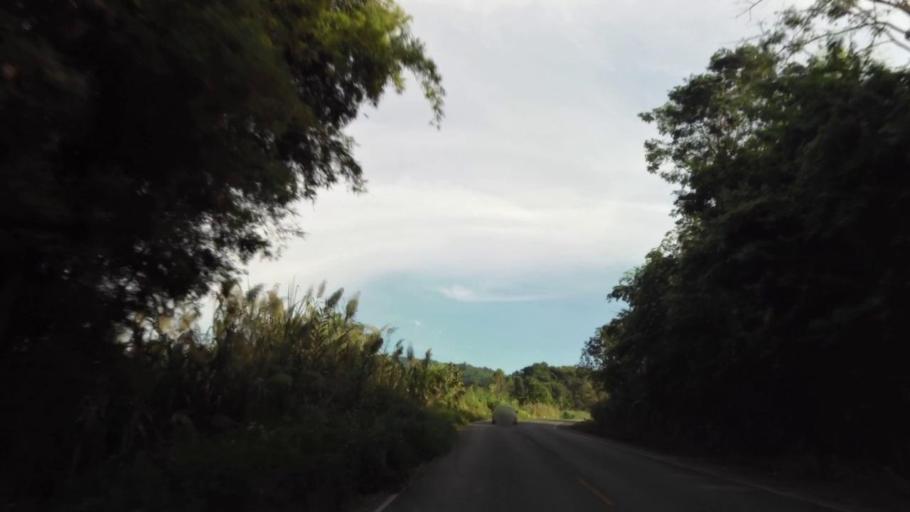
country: TH
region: Chiang Rai
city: Khun Tan
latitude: 19.8648
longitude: 100.4223
